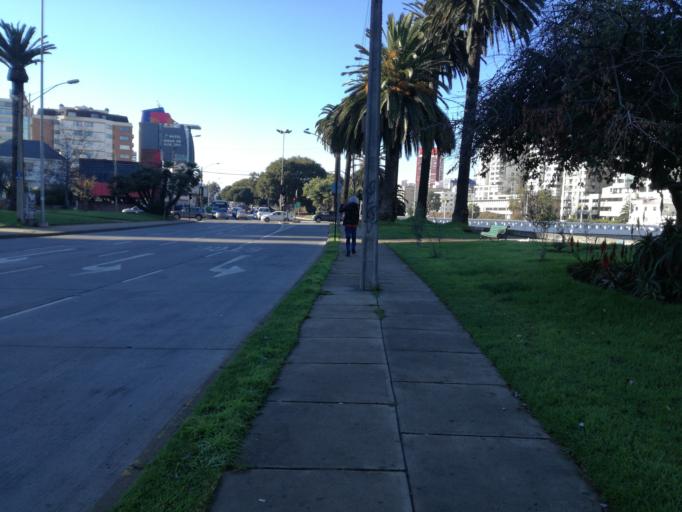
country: CL
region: Valparaiso
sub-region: Provincia de Valparaiso
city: Vina del Mar
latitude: -33.0208
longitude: -71.5597
